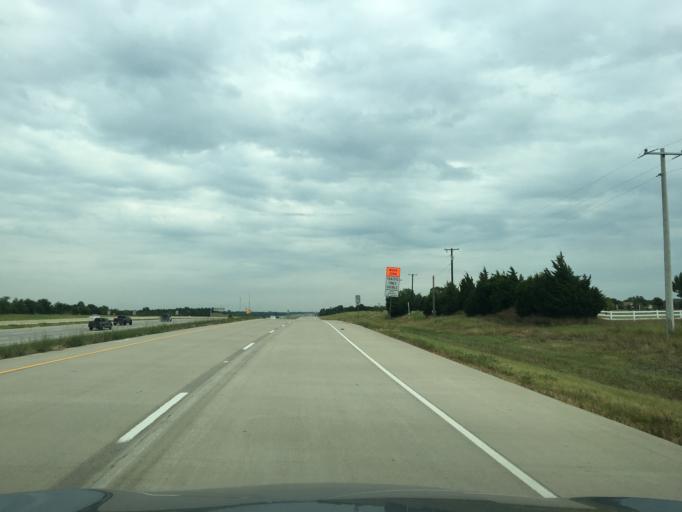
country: US
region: Texas
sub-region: Collin County
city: Melissa
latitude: 33.2876
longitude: -96.5917
